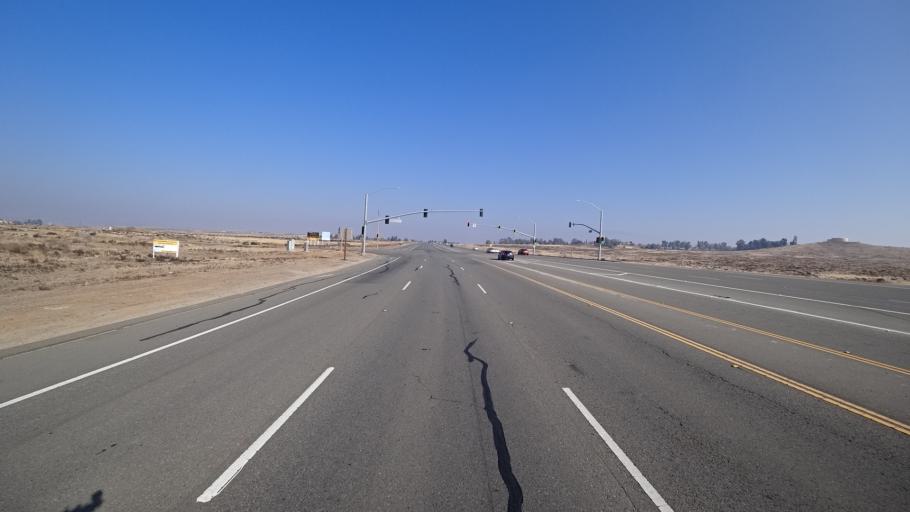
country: US
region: California
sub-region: Kern County
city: Oildale
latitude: 35.3996
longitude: -118.8774
